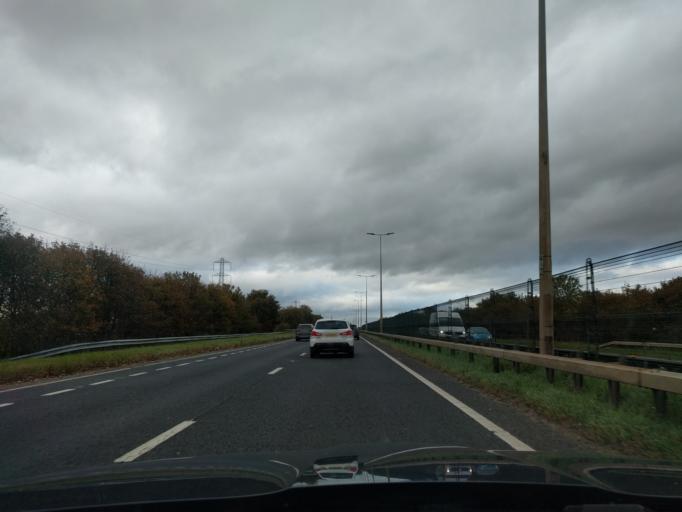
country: GB
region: England
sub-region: Newcastle upon Tyne
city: Hazlerigg
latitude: 55.0404
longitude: -1.6294
